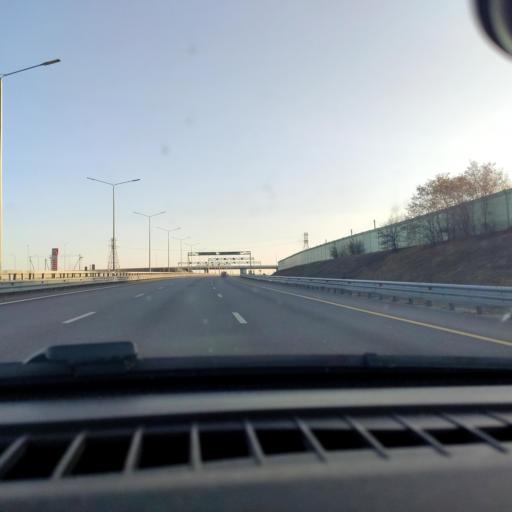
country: RU
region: Voronezj
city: Ramon'
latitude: 51.8257
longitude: 39.2482
